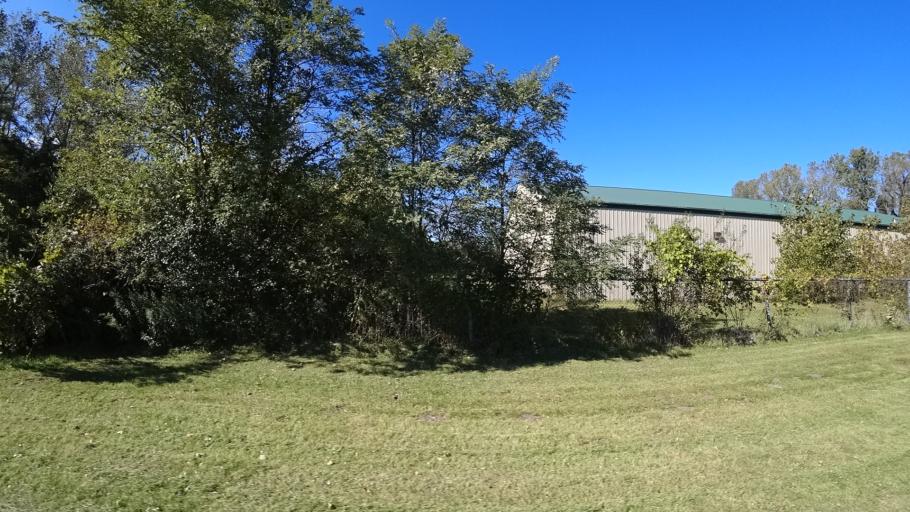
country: US
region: Indiana
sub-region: LaPorte County
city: Michigan City
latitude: 41.7042
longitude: -86.9218
